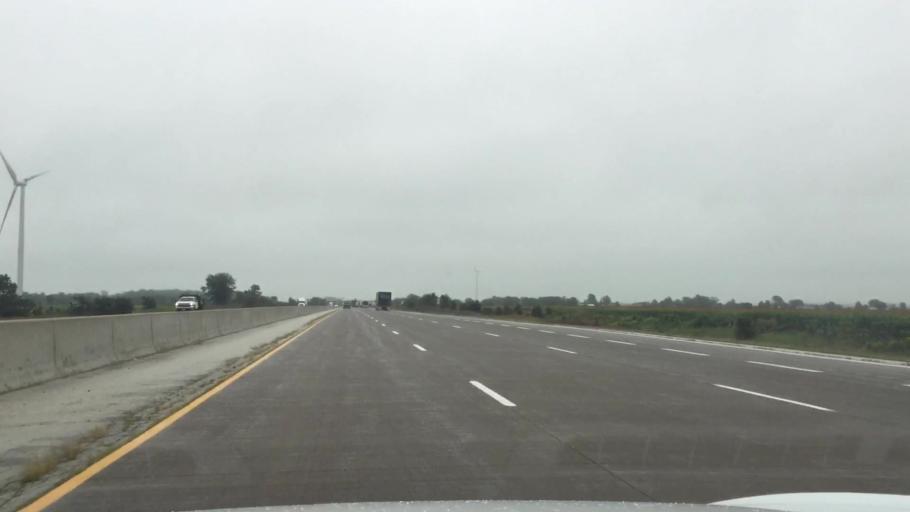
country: US
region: Michigan
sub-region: Wayne County
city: Grosse Pointe Farms
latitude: 42.2366
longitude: -82.7041
